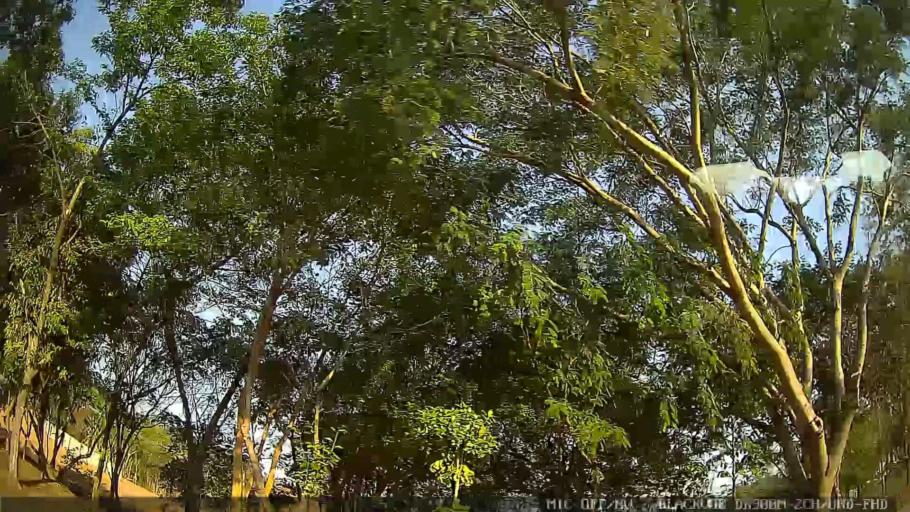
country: BR
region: Sao Paulo
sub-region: Itatiba
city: Itatiba
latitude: -23.0243
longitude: -46.8397
